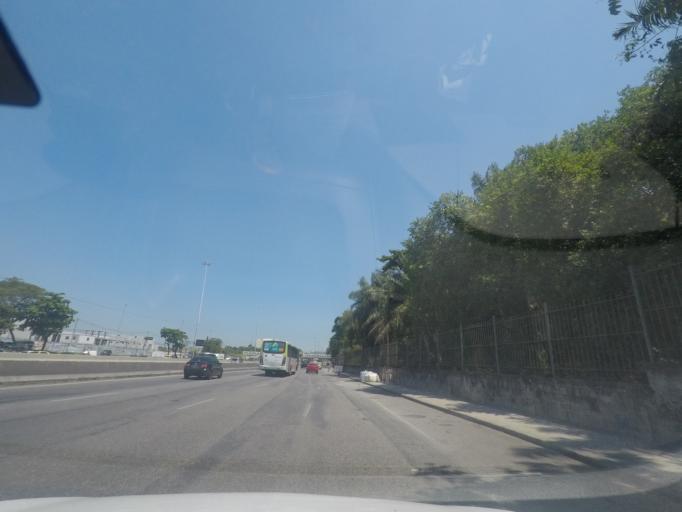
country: BR
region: Rio de Janeiro
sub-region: Rio De Janeiro
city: Rio de Janeiro
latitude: -22.8729
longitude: -43.2452
